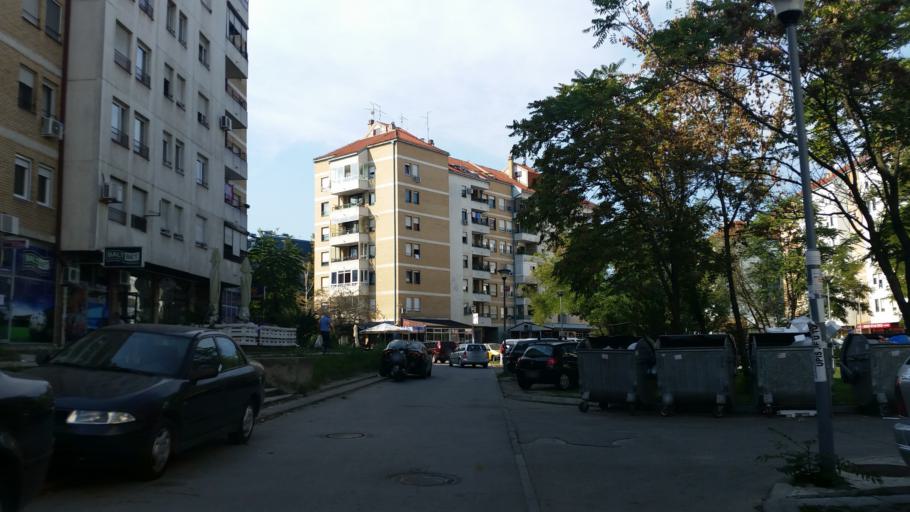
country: RS
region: Central Serbia
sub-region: Belgrade
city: Zemun
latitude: 44.8232
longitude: 20.4029
